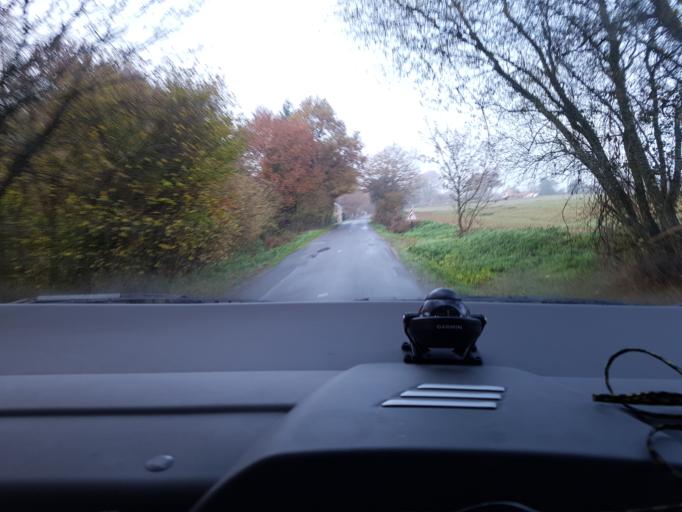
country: FR
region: Brittany
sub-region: Departement d'Ille-et-Vilaine
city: Livre-sur-Changeon
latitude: 48.1892
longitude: -1.3566
